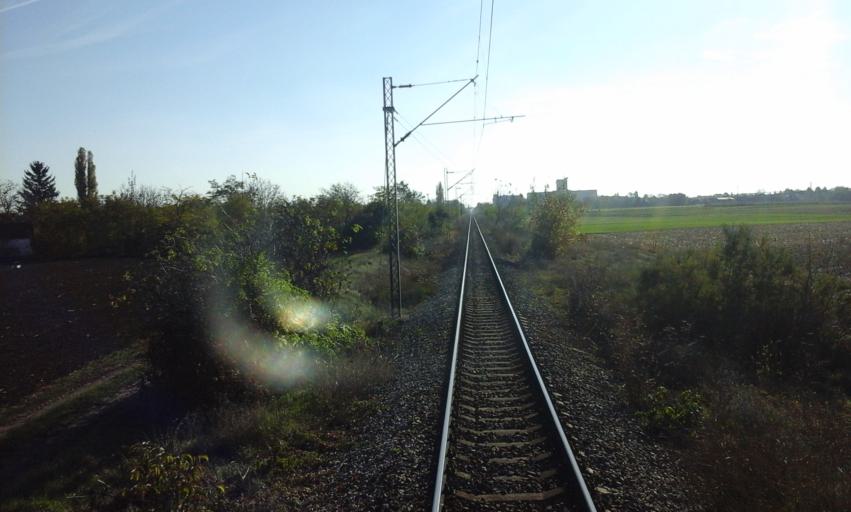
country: RS
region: Autonomna Pokrajina Vojvodina
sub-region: Severnobacki Okrug
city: Backa Topola
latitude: 45.8296
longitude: 19.6513
